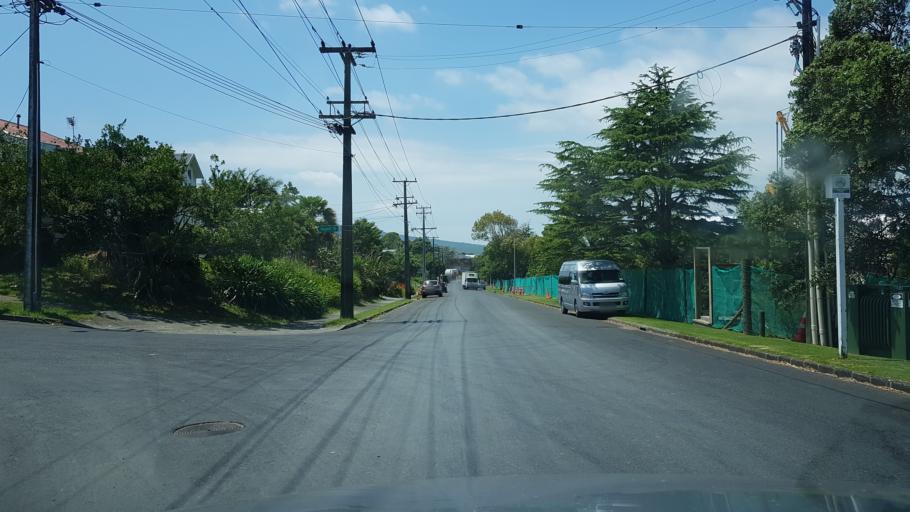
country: NZ
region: Auckland
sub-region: Auckland
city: North Shore
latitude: -36.8168
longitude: 174.7910
